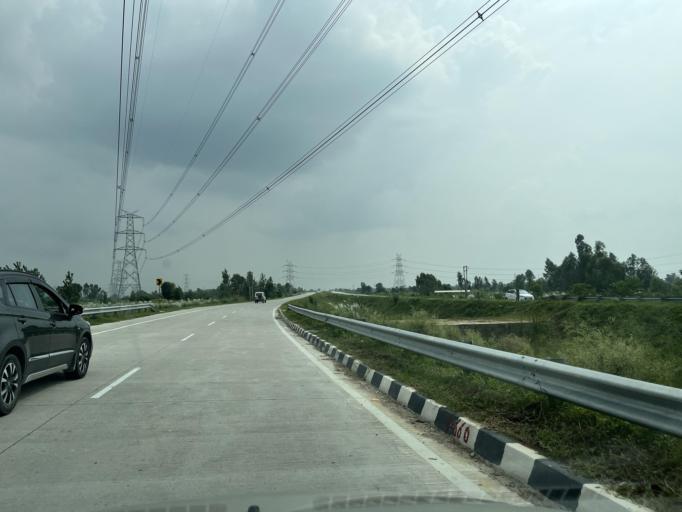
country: IN
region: Uttarakhand
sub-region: Udham Singh Nagar
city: Jaspur
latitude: 29.2773
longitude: 78.8681
